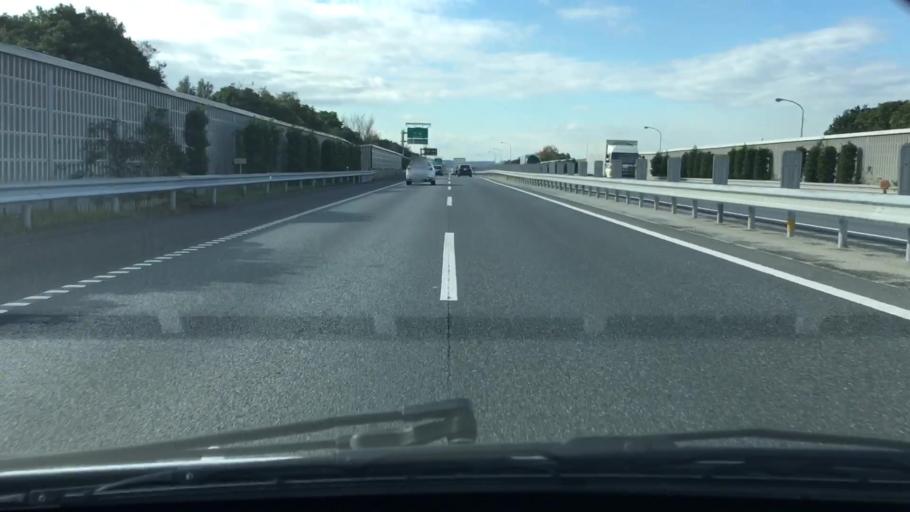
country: JP
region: Chiba
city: Ichihara
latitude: 35.5002
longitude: 140.0981
